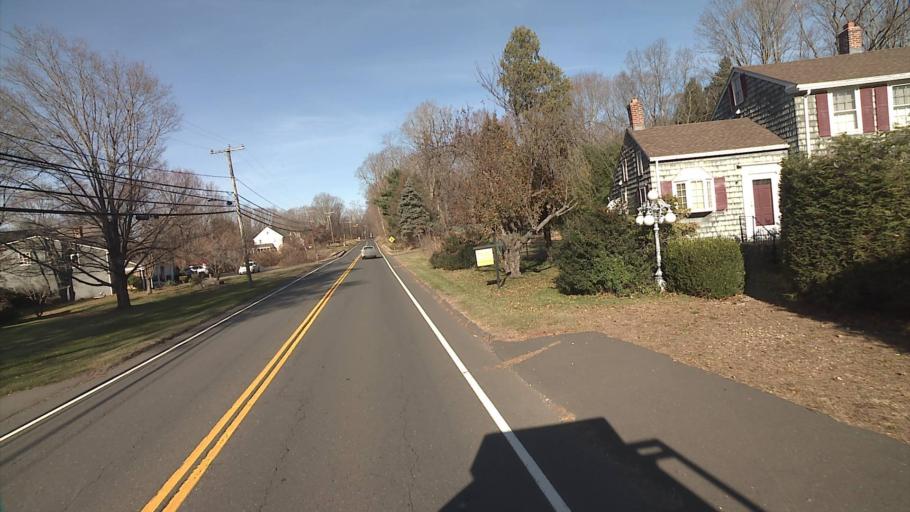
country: US
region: Connecticut
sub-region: Middlesex County
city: Cromwell
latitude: 41.6185
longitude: -72.5998
